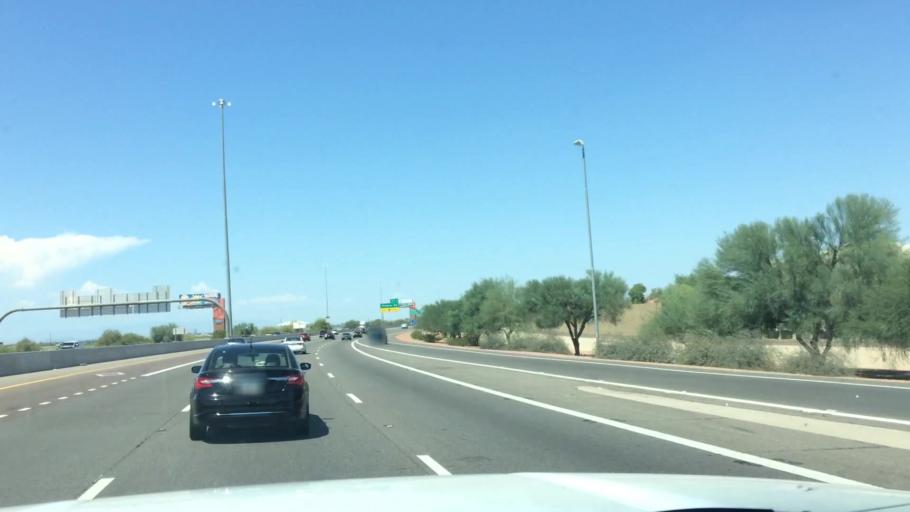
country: US
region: Arizona
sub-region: Maricopa County
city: Tolleson
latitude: 33.4684
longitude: -112.2680
